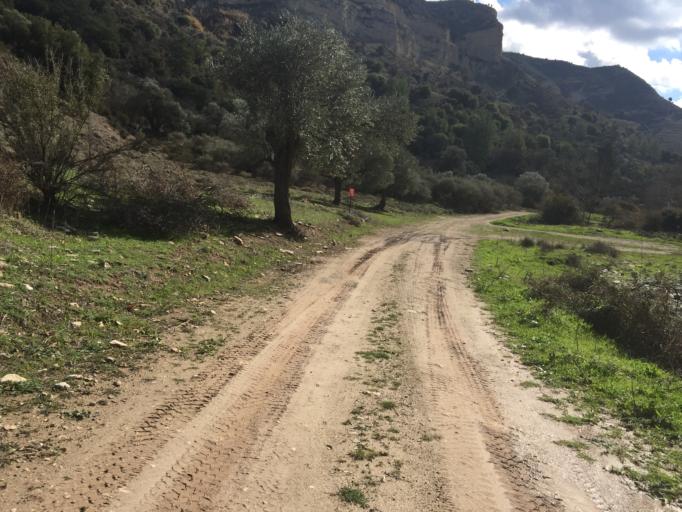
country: CY
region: Limassol
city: Pachna
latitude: 34.8820
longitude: 32.6769
